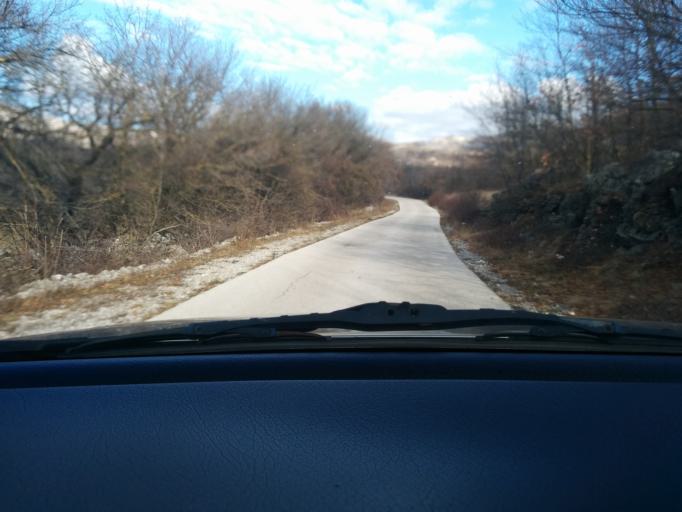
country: HR
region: Splitsko-Dalmatinska
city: Hrvace
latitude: 43.8110
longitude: 16.6921
